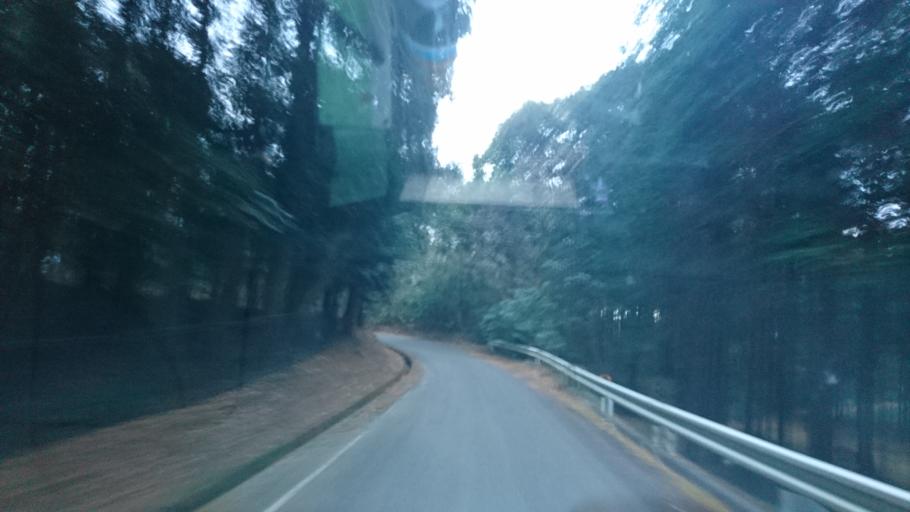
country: JP
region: Shizuoka
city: Fujinomiya
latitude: 35.3325
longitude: 138.5771
